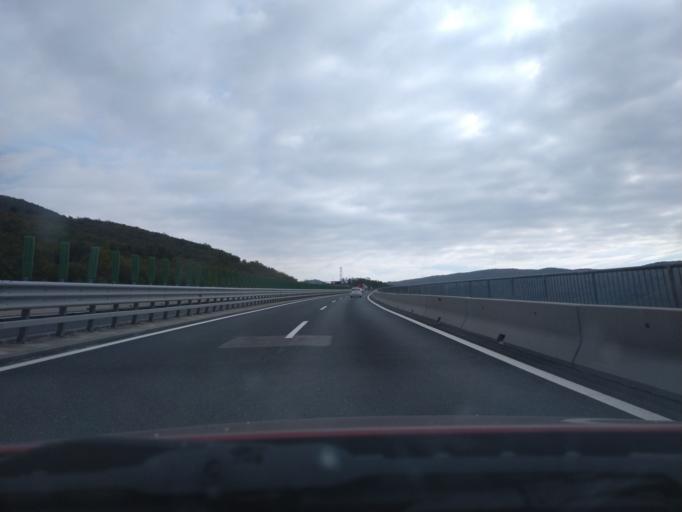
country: SI
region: Vipava
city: Vipava
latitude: 45.7768
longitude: 14.0204
